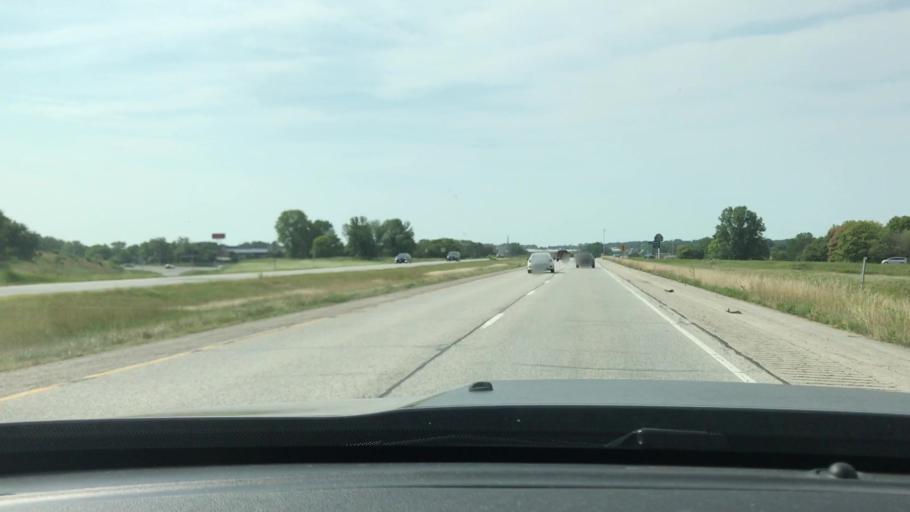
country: US
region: Iowa
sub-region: Scott County
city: Bettendorf
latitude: 41.5584
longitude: -90.5225
